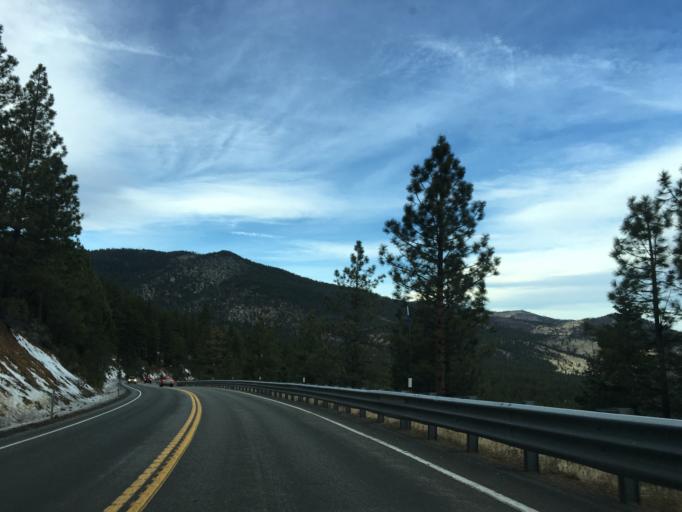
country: US
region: Nevada
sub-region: Washoe County
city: Incline Village
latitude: 39.3477
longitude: -119.8491
